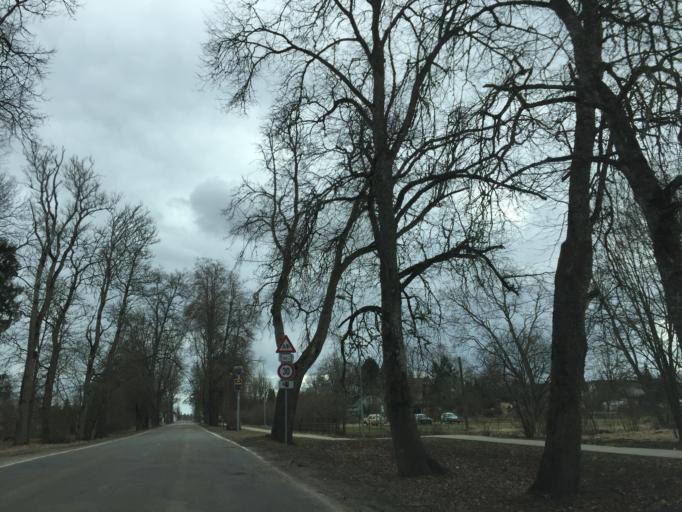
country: LV
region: Ropazu
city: Ropazi
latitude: 56.9763
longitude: 24.6322
